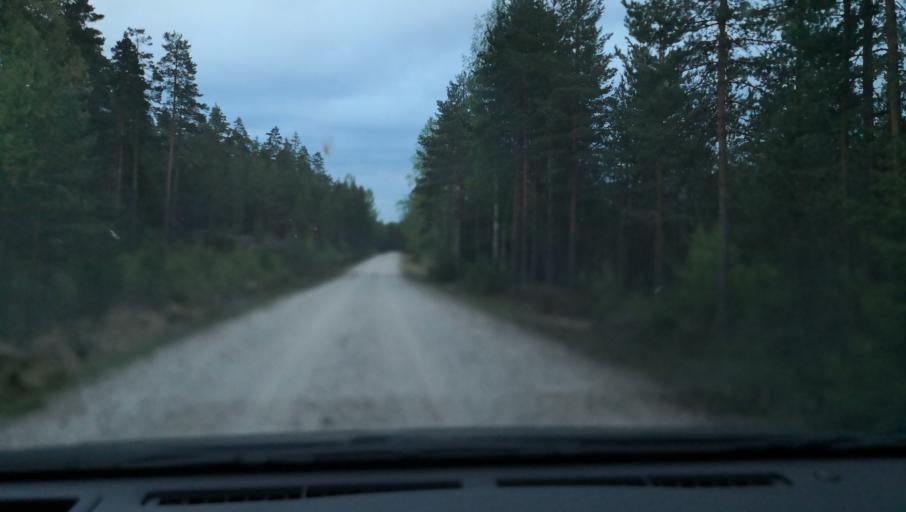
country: SE
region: Vaestmanland
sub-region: Skinnskattebergs Kommun
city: Skinnskatteberg
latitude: 59.7636
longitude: 15.4583
